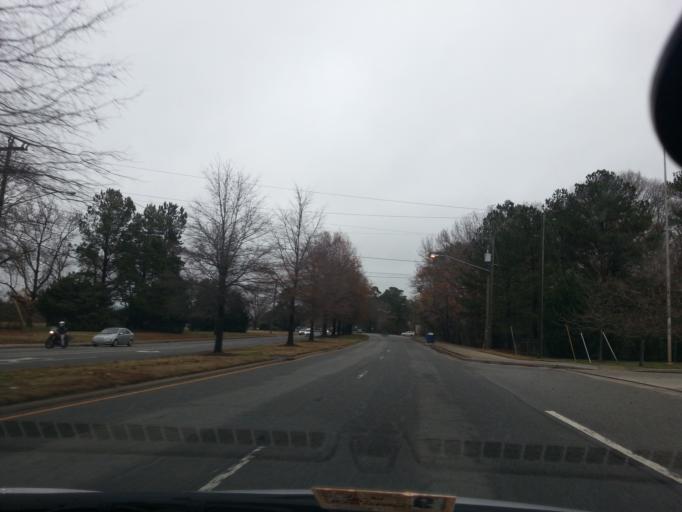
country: US
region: Virginia
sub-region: City of Virginia Beach
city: Virginia Beach
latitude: 36.7754
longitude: -76.0059
